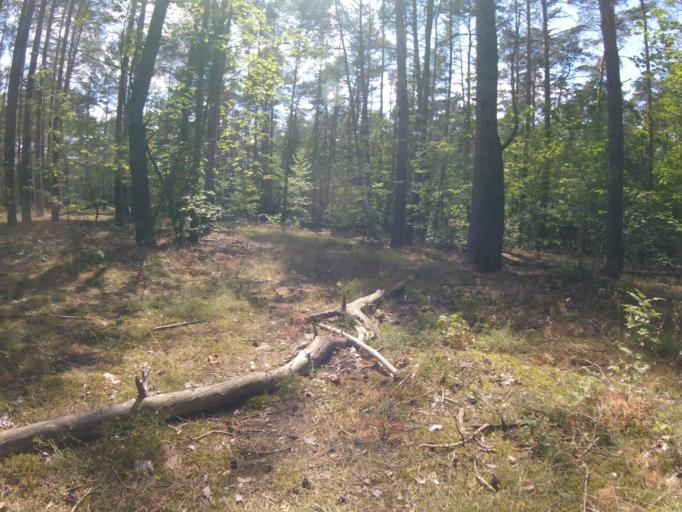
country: DE
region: Brandenburg
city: Wildau
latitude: 52.3264
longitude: 13.6652
